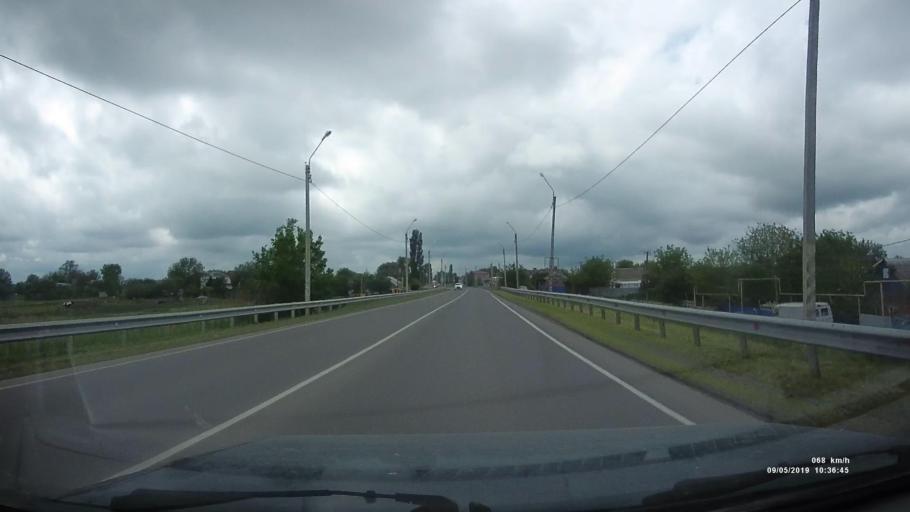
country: RU
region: Rostov
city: Peshkovo
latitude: 47.0262
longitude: 39.4062
